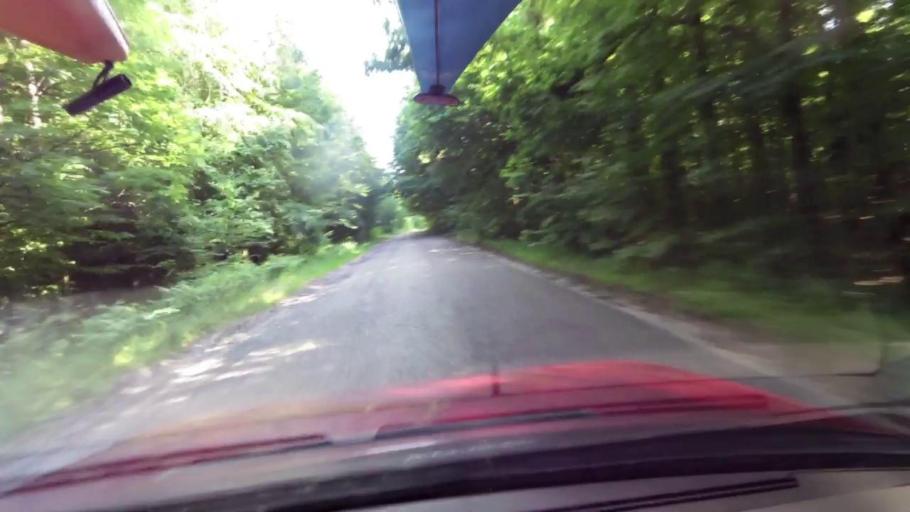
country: PL
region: Pomeranian Voivodeship
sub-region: Powiat slupski
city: Kepice
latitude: 54.1598
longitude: 16.9076
